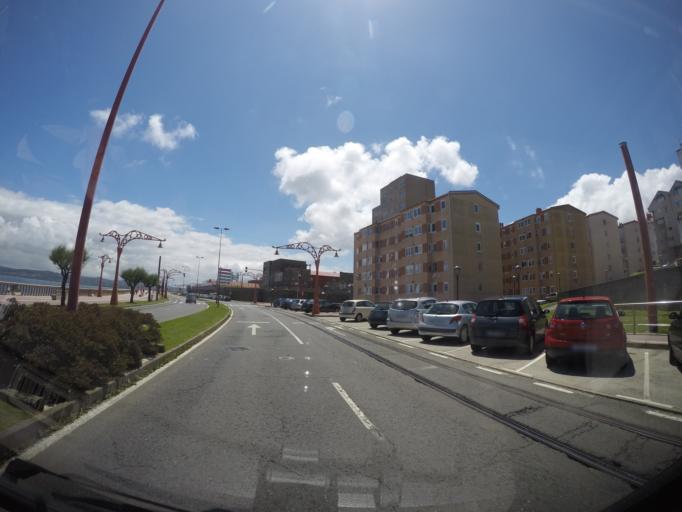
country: ES
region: Galicia
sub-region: Provincia da Coruna
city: A Coruna
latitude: 43.3714
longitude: -8.3897
